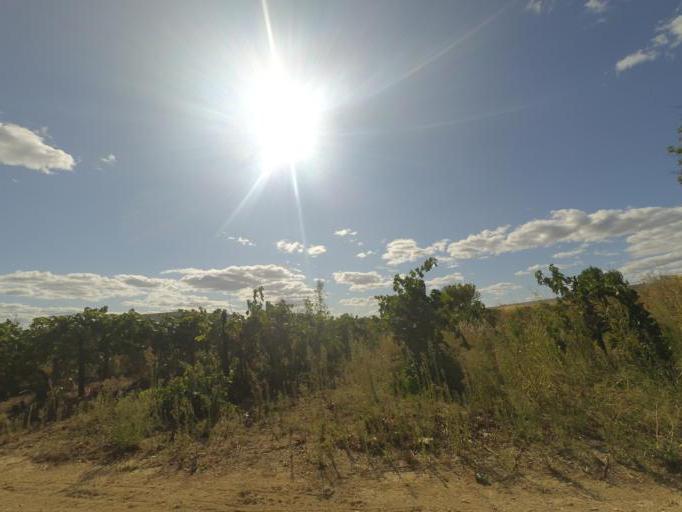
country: FR
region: Languedoc-Roussillon
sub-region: Departement du Gard
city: Vergeze
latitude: 43.7383
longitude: 4.2176
